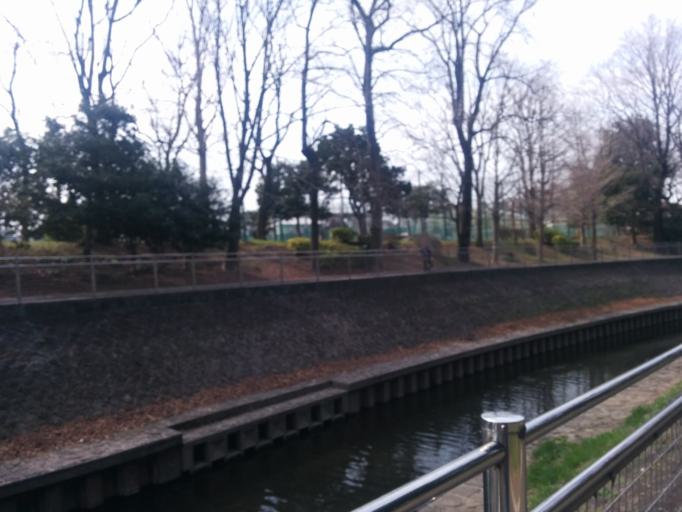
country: JP
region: Tokyo
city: Tokyo
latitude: 35.6898
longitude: 139.6327
